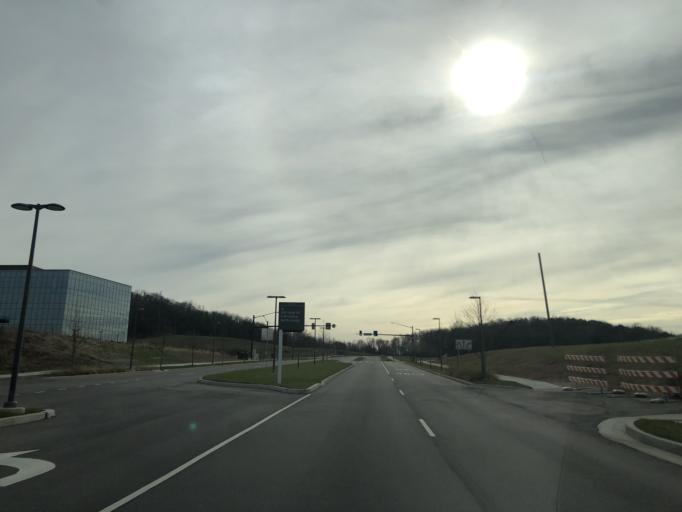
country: US
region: Tennessee
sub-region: Williamson County
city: Franklin
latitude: 35.9316
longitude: -86.8062
